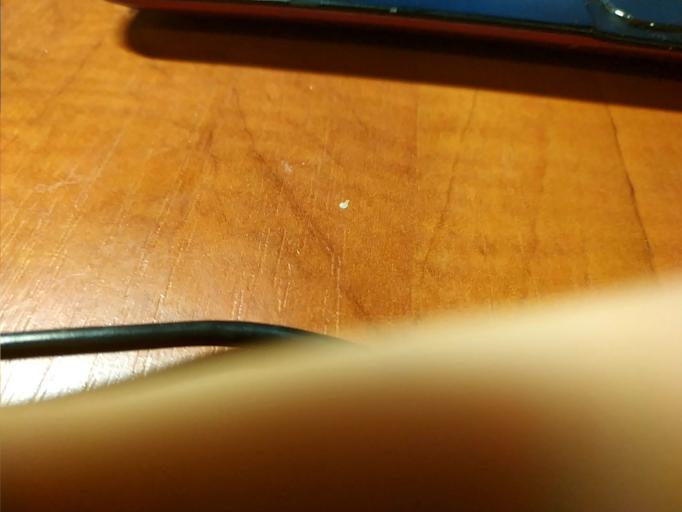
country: RU
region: Tverskaya
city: Likhoslavl'
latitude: 57.0111
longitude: 35.6165
